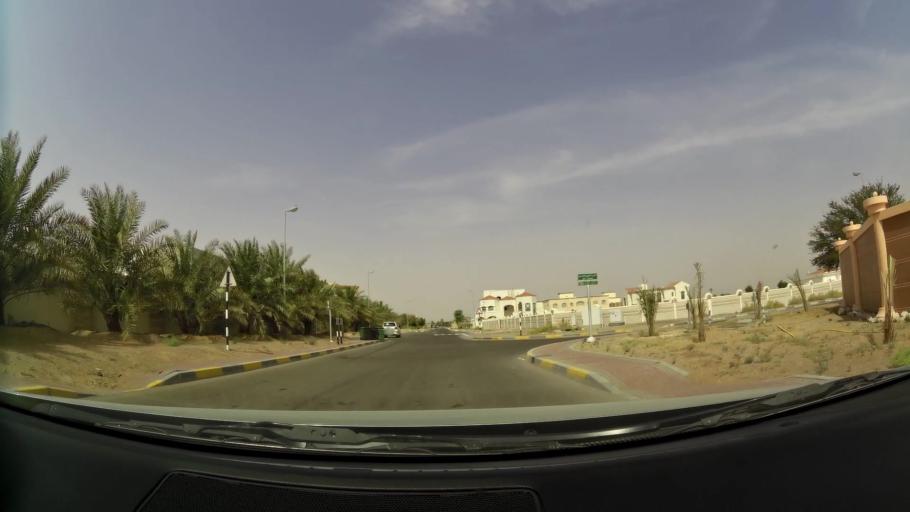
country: AE
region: Abu Dhabi
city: Al Ain
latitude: 24.1597
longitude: 55.6782
